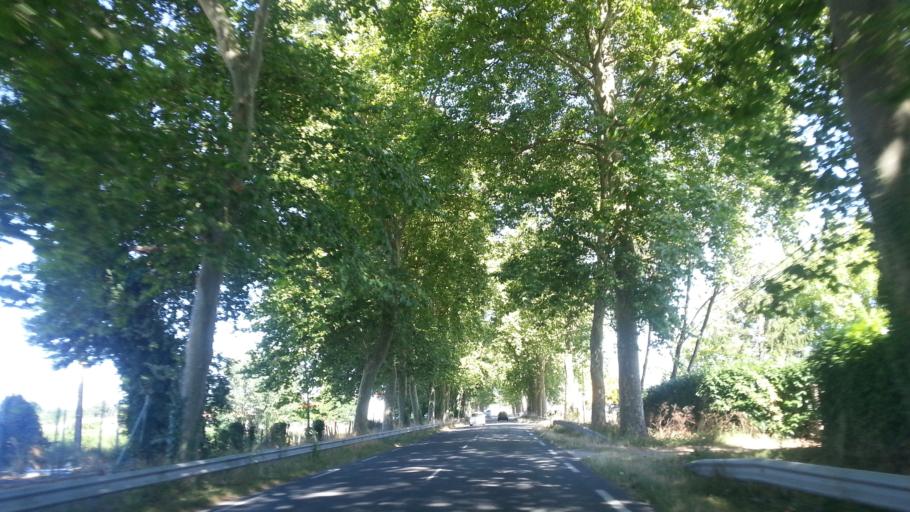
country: FR
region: Aquitaine
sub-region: Departement de la Gironde
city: Martillac
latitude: 44.7315
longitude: -0.5326
